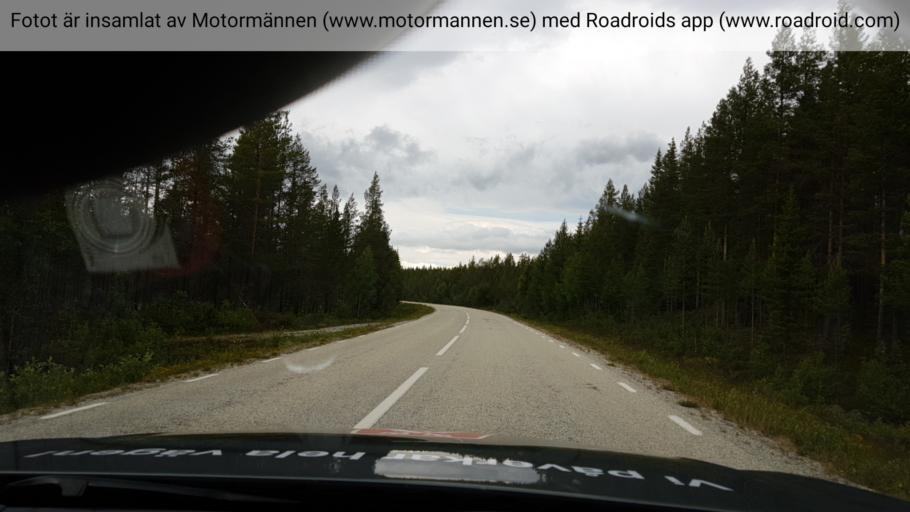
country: SE
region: Jaemtland
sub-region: Are Kommun
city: Jarpen
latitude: 62.8214
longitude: 13.5040
